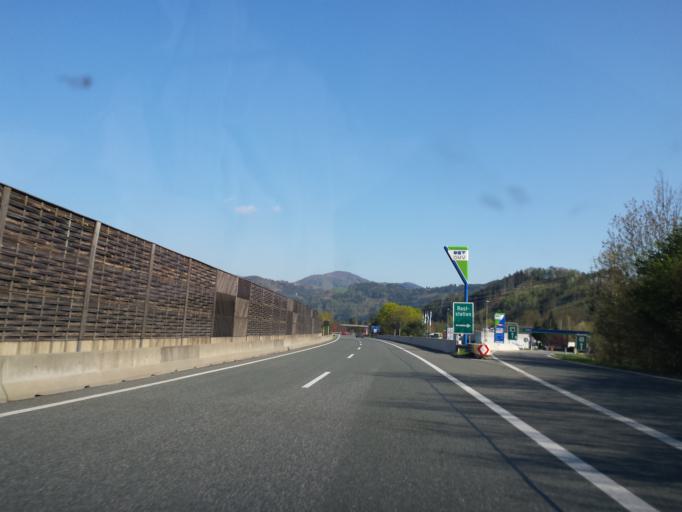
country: AT
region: Styria
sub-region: Politischer Bezirk Graz-Umgebung
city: Deutschfeistritz
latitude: 47.2066
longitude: 15.3141
